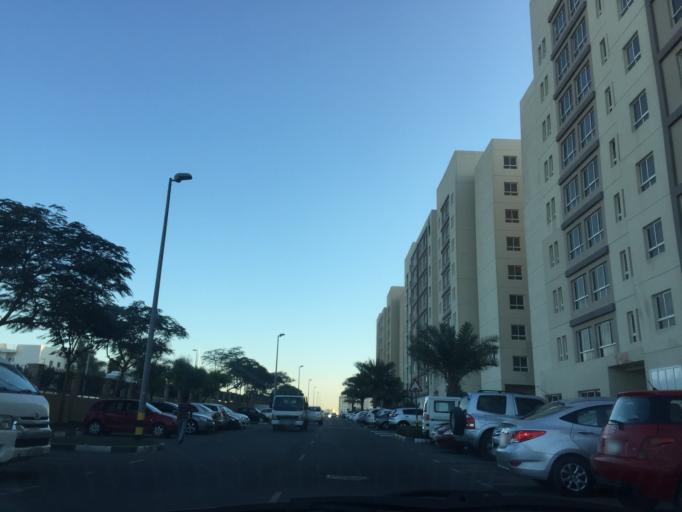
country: AE
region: Dubai
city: Dubai
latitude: 25.1406
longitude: 55.2473
